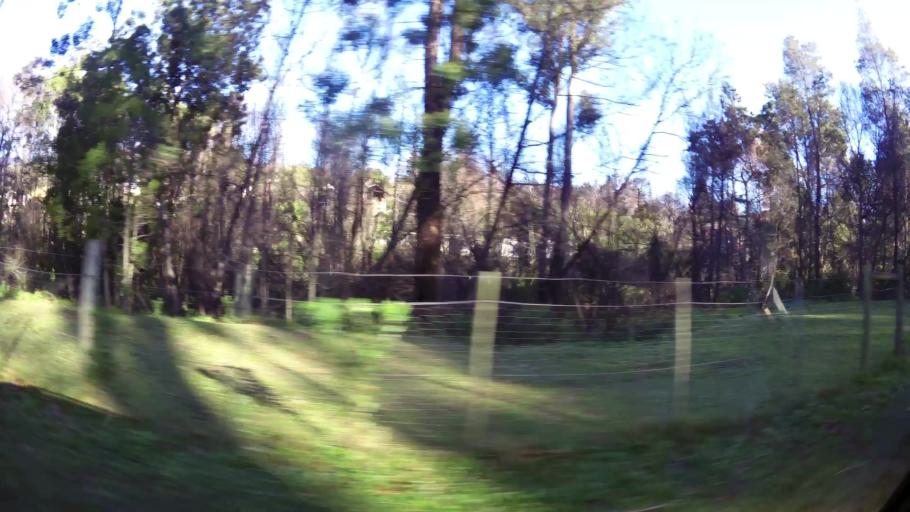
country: ZA
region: Western Cape
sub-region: Eden District Municipality
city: Knysna
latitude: -34.0326
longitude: 23.0148
